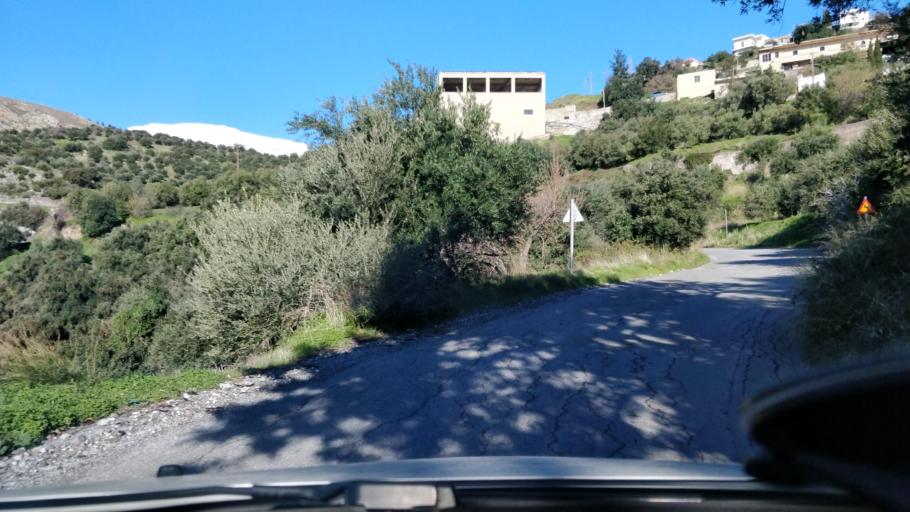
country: GR
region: Crete
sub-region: Nomos Lasithiou
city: Kritsa
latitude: 35.0776
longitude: 25.5830
